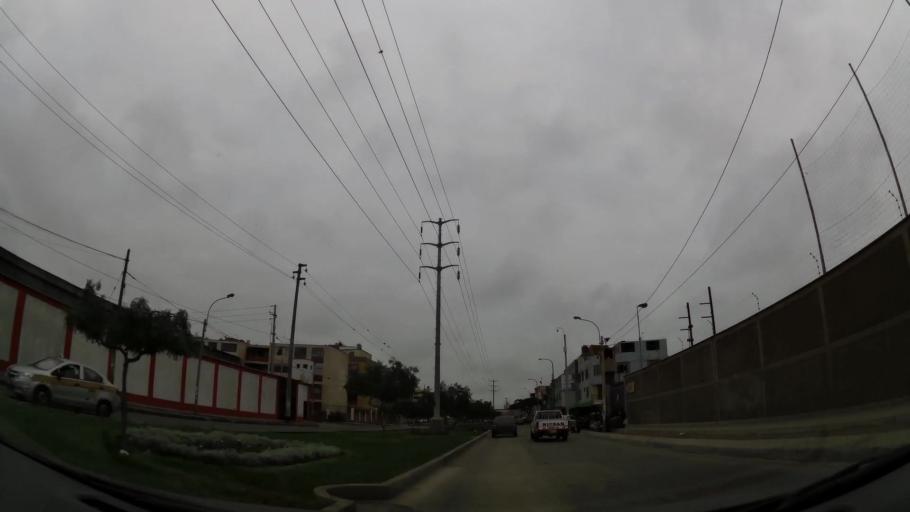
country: PE
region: Lima
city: Lima
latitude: -12.0583
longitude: -77.0636
